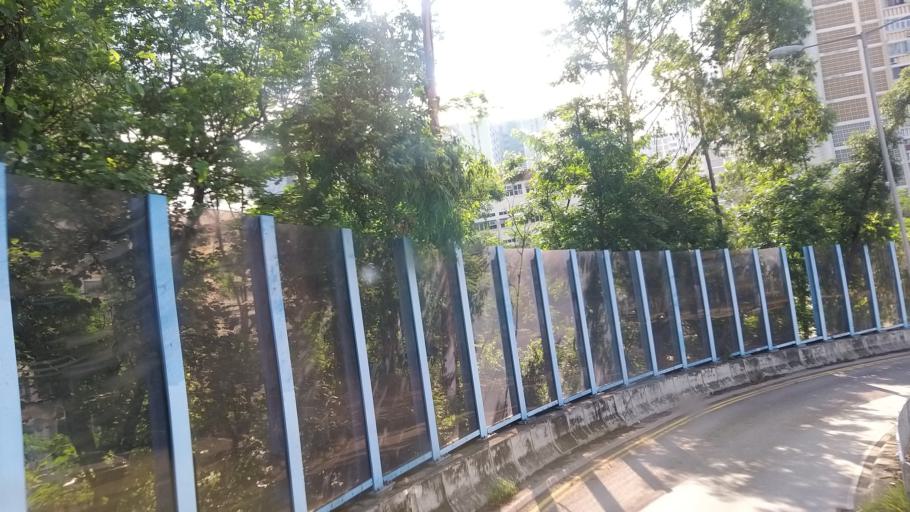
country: HK
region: Tuen Mun
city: Tuen Mun
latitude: 22.3867
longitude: 113.9715
